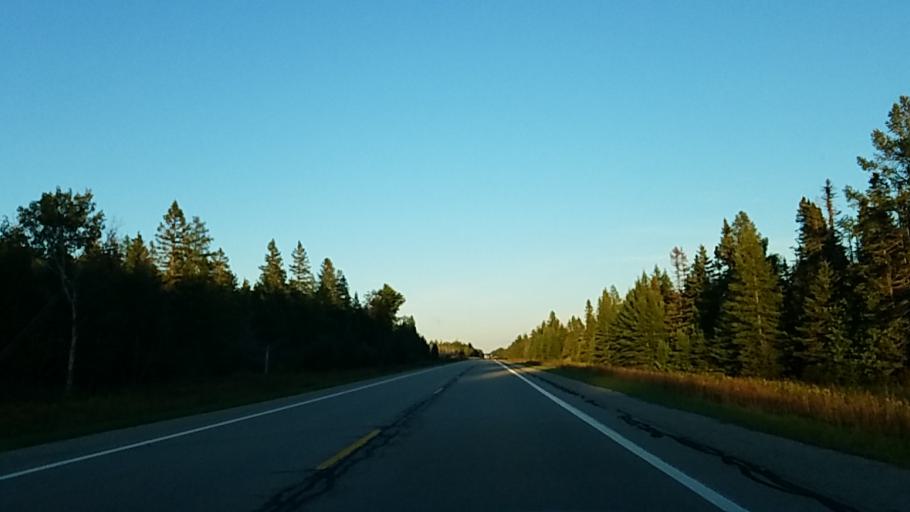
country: US
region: Michigan
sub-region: Alger County
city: Munising
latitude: 46.3467
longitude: -86.3802
